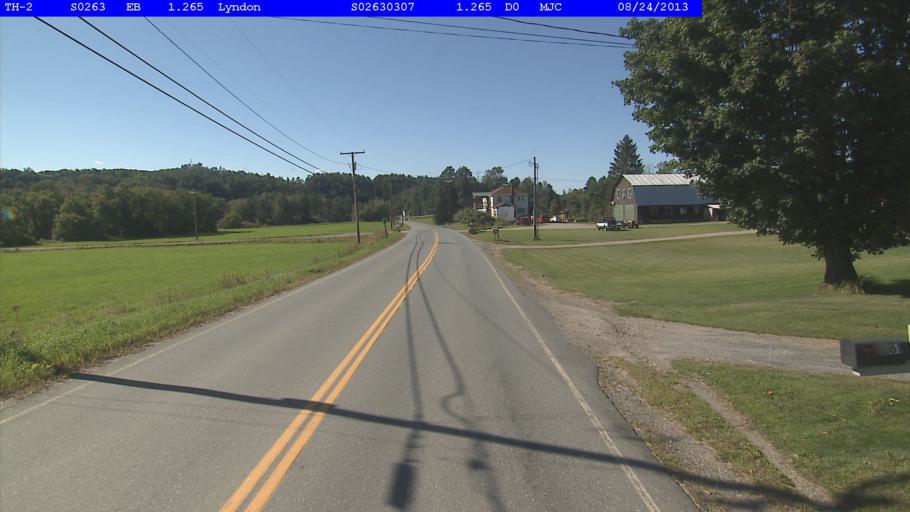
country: US
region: Vermont
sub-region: Caledonia County
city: Lyndon
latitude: 44.5049
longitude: -71.9860
